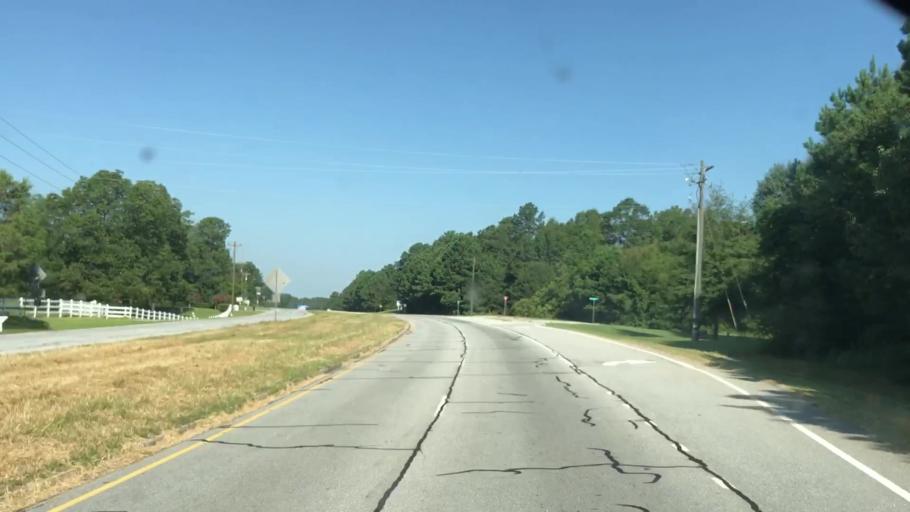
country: US
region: Georgia
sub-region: Walton County
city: Walnut Grove
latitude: 33.8199
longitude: -83.8100
